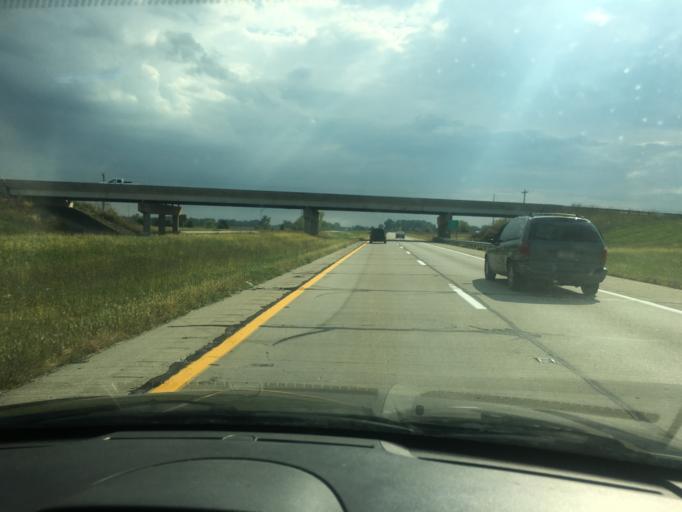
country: US
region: Ohio
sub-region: Clark County
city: Northridge
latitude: 40.0279
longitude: -83.8038
